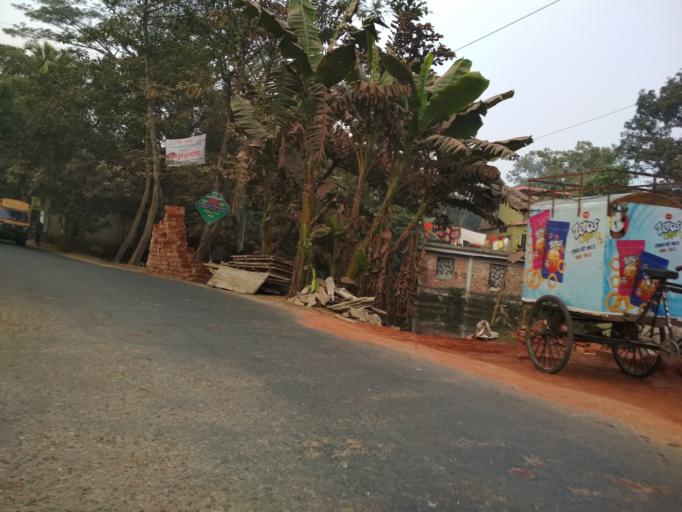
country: BD
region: Chittagong
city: Lakshmipur
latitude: 22.9208
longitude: 90.8375
